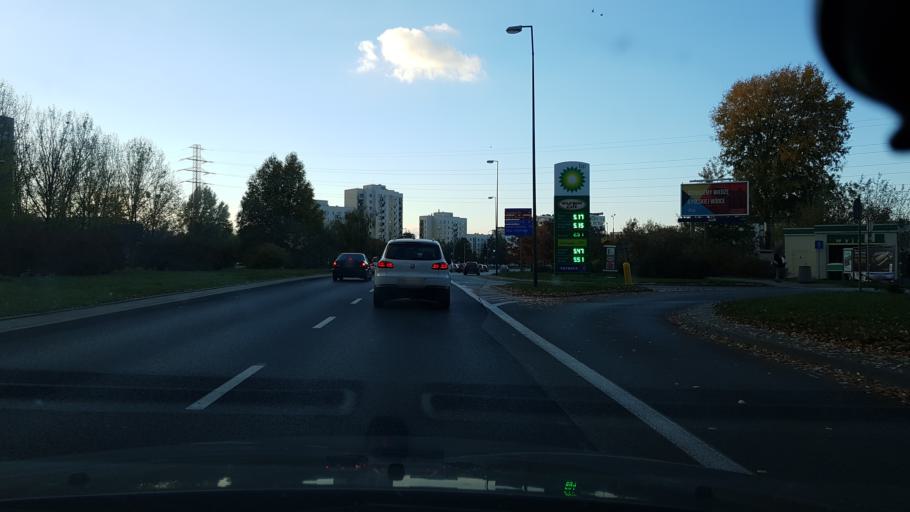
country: PL
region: Masovian Voivodeship
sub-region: Warszawa
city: Ursynow
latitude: 52.1560
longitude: 21.0468
